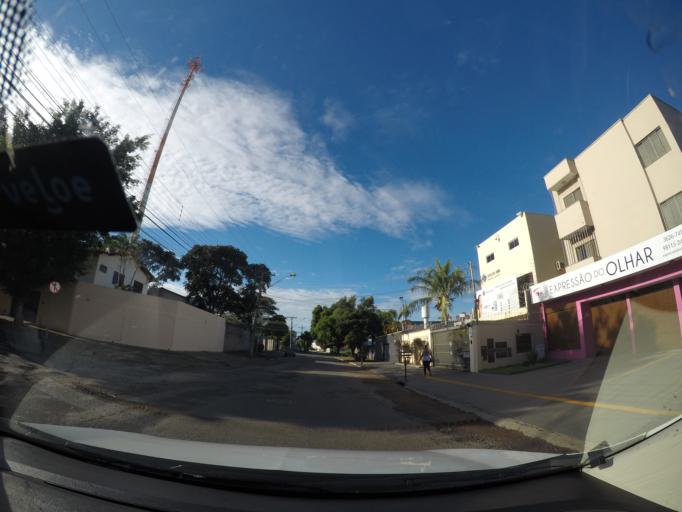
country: BR
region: Goias
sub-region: Goiania
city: Goiania
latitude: -16.7225
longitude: -49.2688
